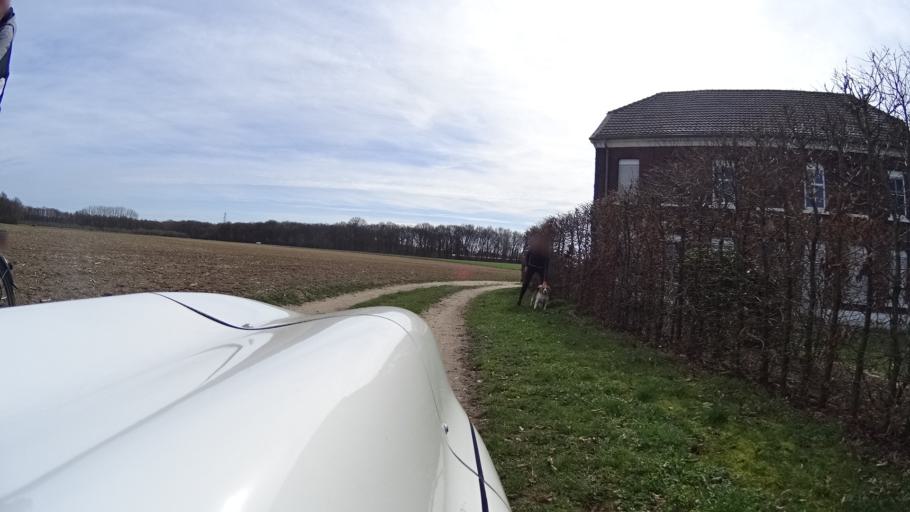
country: DE
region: North Rhine-Westphalia
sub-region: Regierungsbezirk Dusseldorf
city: Kevelaer
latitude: 51.6017
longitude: 6.2481
